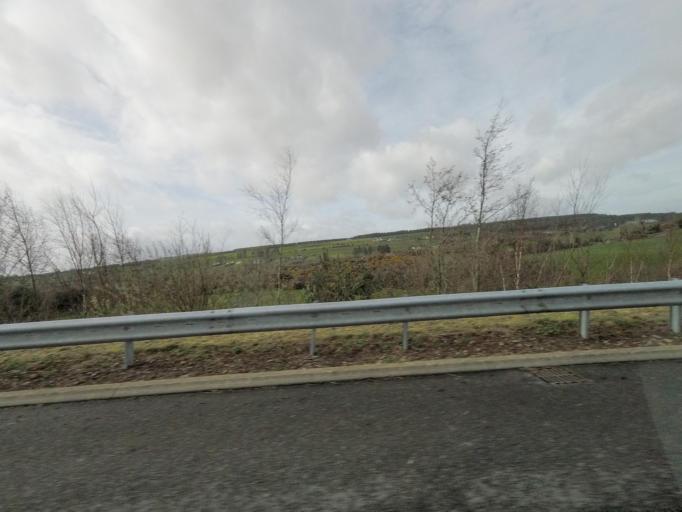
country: IE
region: Leinster
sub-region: Kilkenny
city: Thomastown
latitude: 52.4357
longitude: -7.2342
